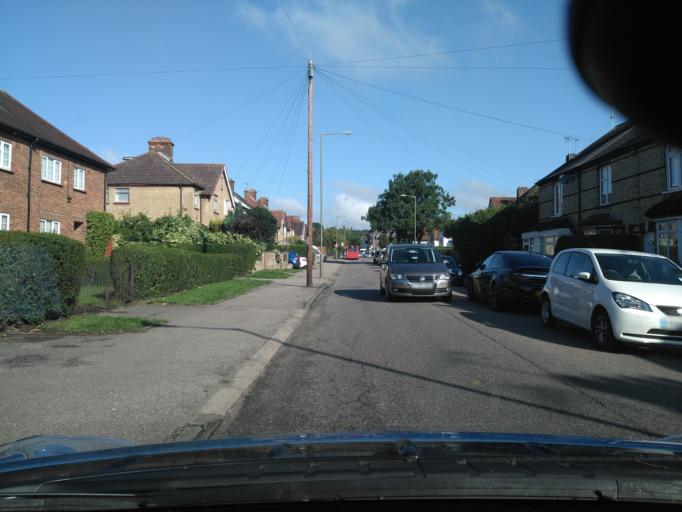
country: GB
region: England
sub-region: Greater London
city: High Barnet
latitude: 51.6454
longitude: -0.2135
